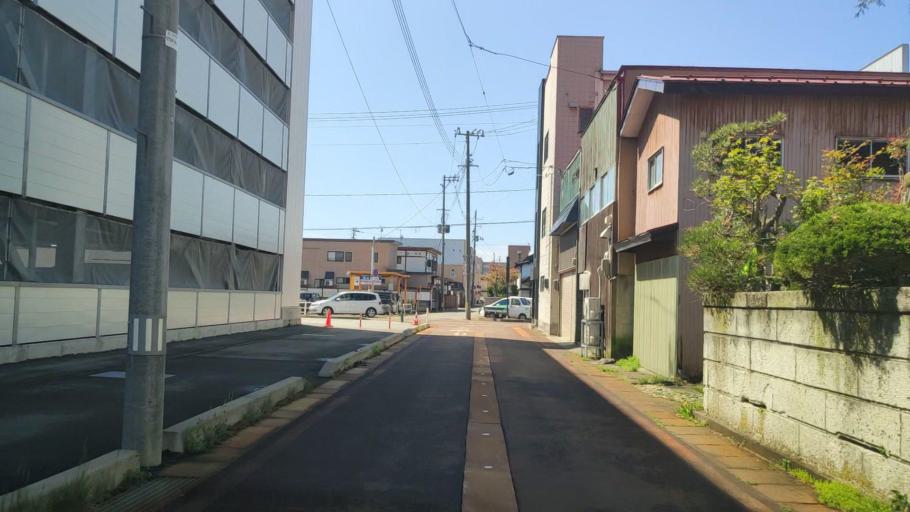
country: JP
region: Akita
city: Omagari
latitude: 39.4640
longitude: 140.4769
